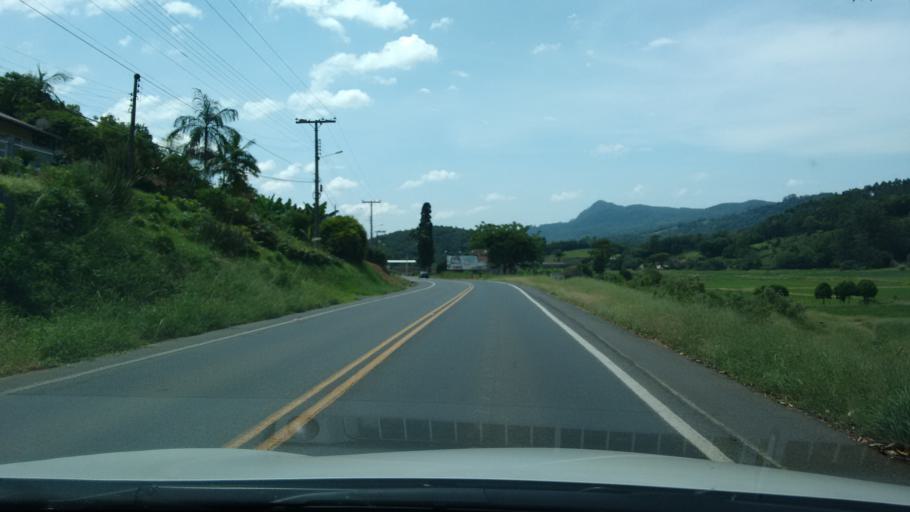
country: BR
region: Santa Catarina
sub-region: Rodeio
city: Gavea
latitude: -26.8916
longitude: -49.3507
